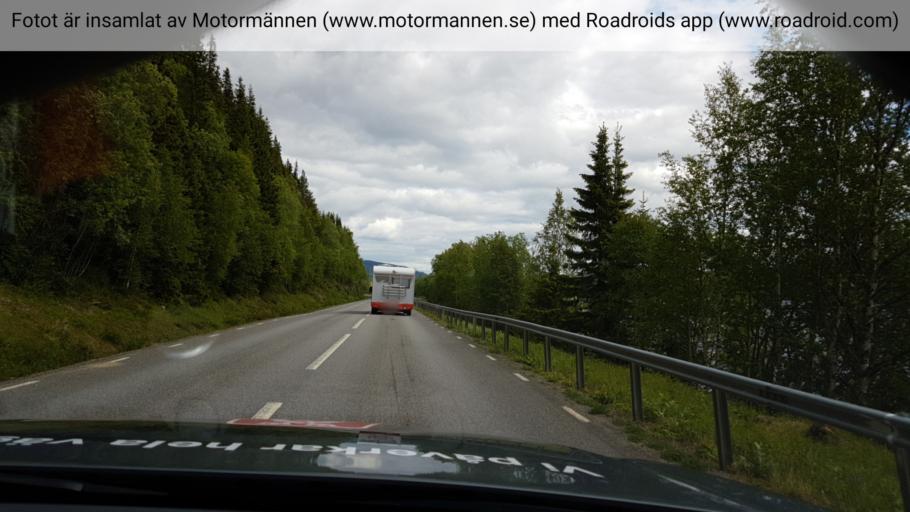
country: NO
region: Nord-Trondelag
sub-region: Lierne
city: Sandvika
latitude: 64.3836
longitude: 14.5458
